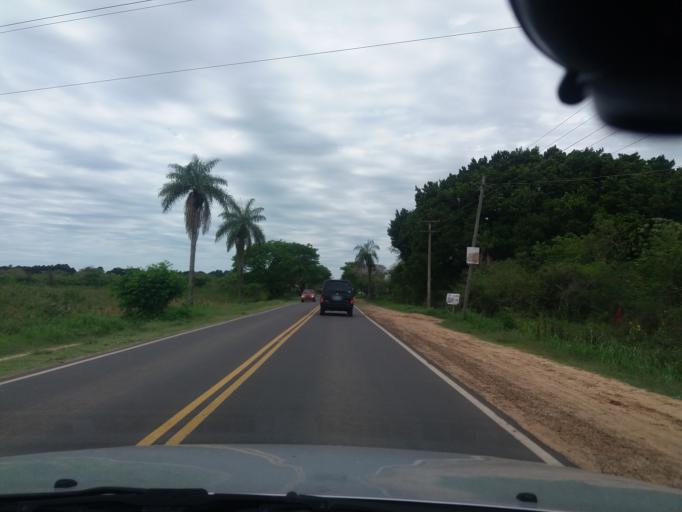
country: AR
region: Corrientes
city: Corrientes
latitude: -27.4500
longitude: -58.7410
